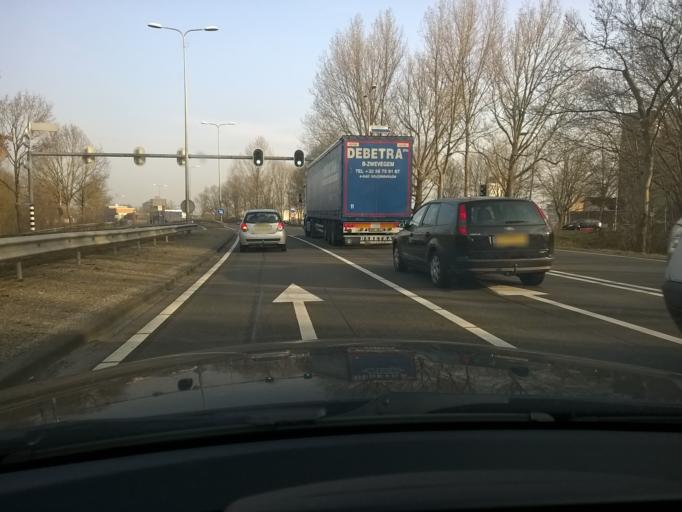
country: NL
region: Groningen
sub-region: Gemeente Groningen
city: Groningen
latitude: 53.2200
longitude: 6.5398
